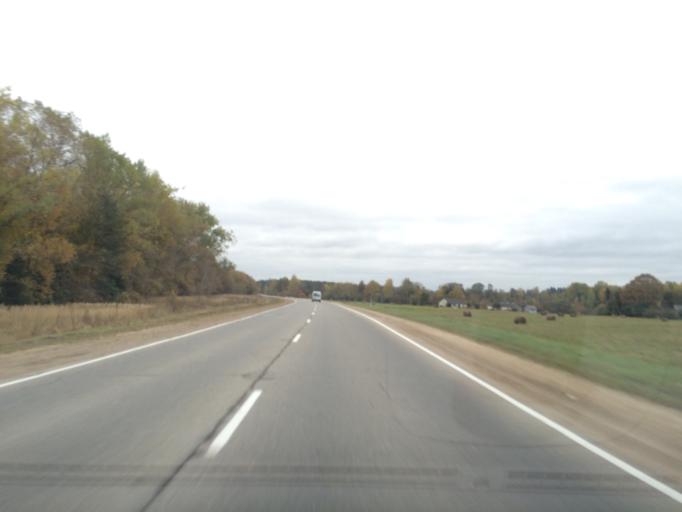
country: LV
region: Koknese
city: Koknese
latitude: 56.6072
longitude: 25.5063
